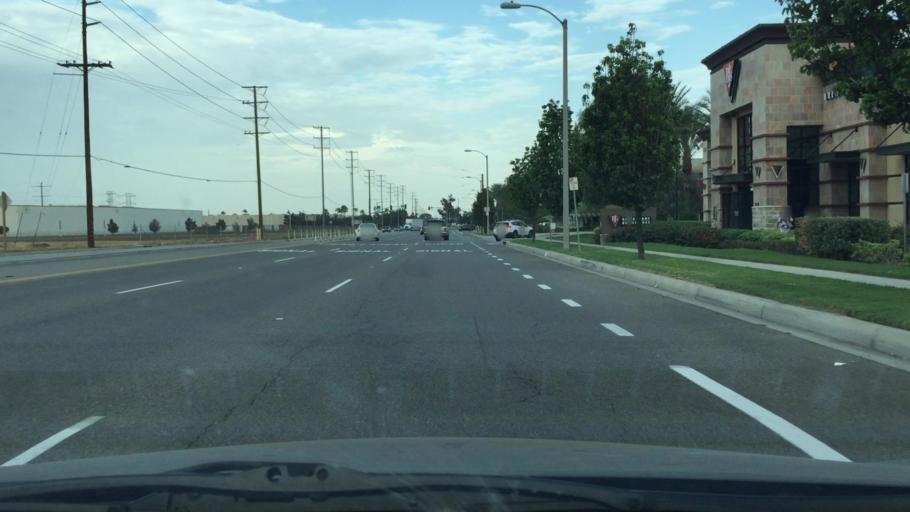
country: US
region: California
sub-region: San Bernardino County
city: Los Serranos
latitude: 33.9826
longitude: -117.7050
